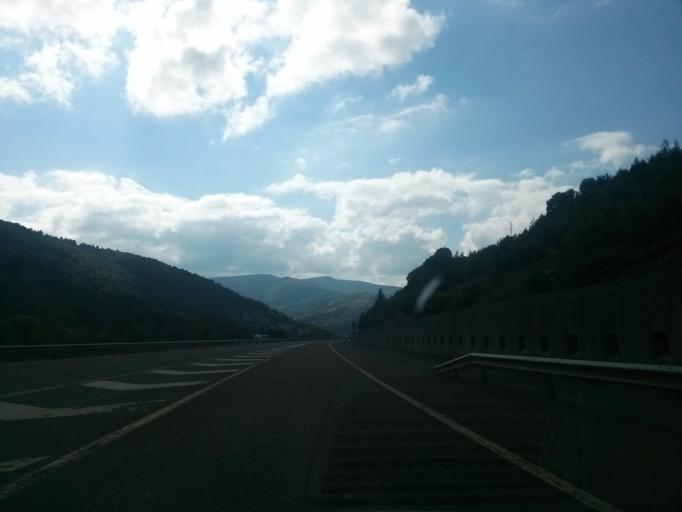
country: ES
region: Castille and Leon
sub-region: Provincia de Leon
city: Balboa
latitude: 42.7268
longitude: -7.0328
